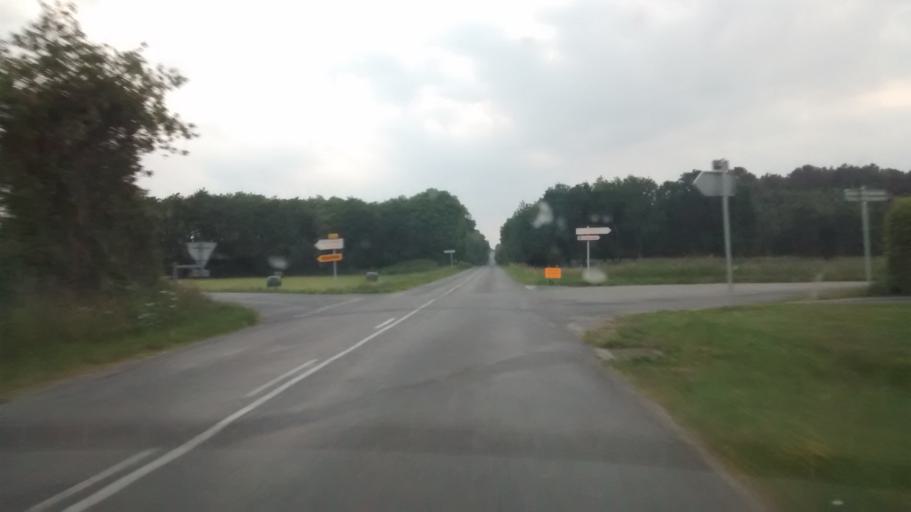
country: FR
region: Brittany
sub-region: Departement du Morbihan
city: Saint-Martin-sur-Oust
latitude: 47.7297
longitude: -2.2909
